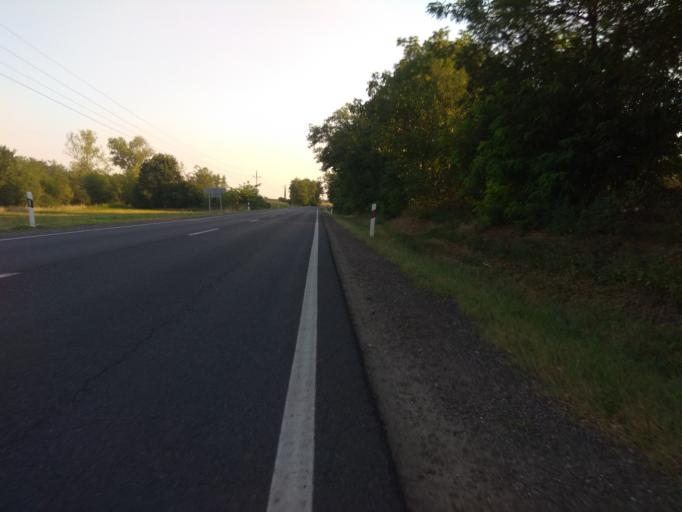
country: HU
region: Borsod-Abauj-Zemplen
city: Emod
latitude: 47.9496
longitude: 20.8327
